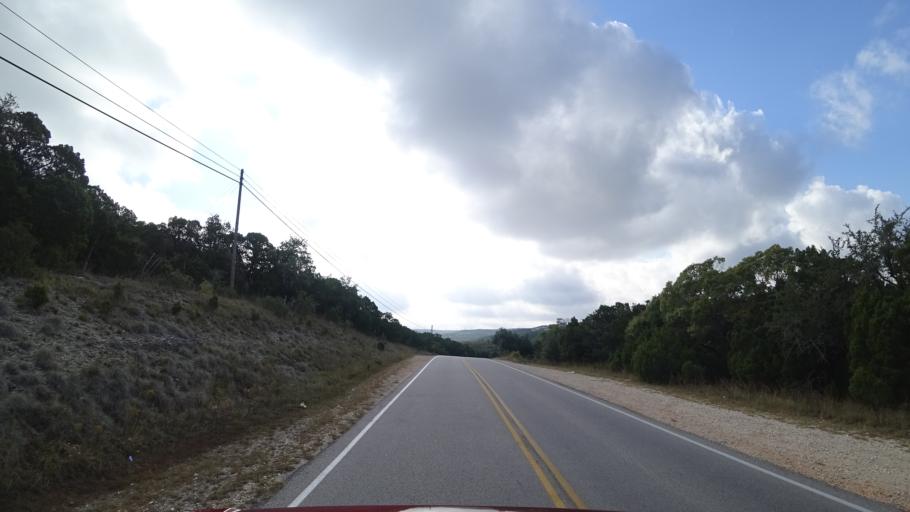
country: US
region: Texas
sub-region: Travis County
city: Hudson Bend
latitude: 30.4194
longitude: -97.8691
